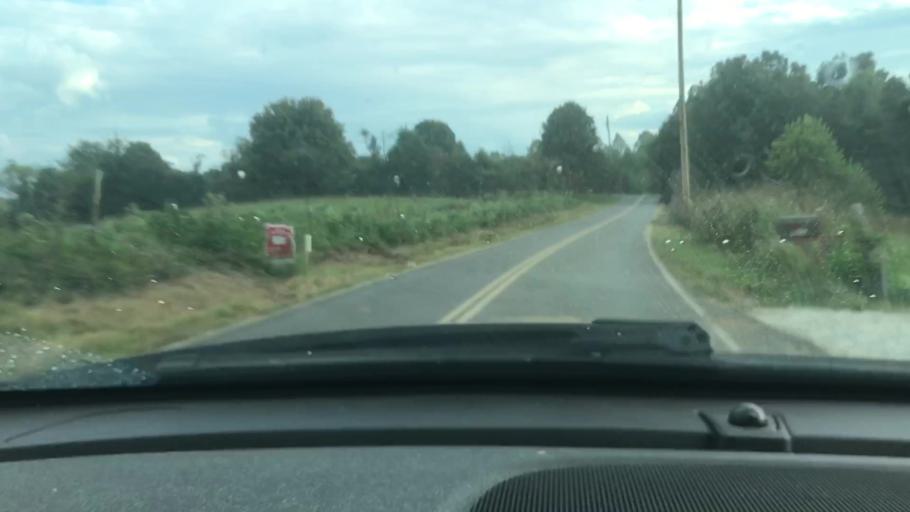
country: US
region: Tennessee
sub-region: Dickson County
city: Charlotte
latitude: 36.1960
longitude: -87.2935
